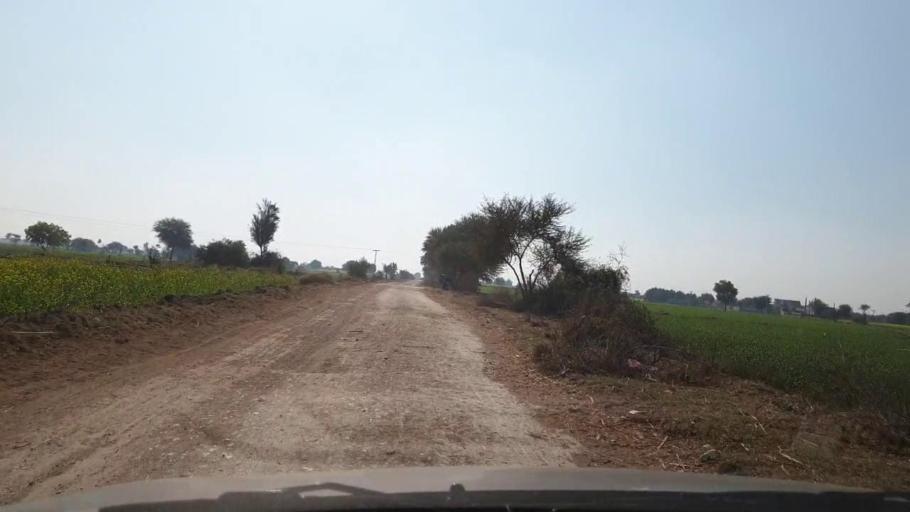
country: PK
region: Sindh
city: Jhol
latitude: 25.9371
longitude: 68.8003
